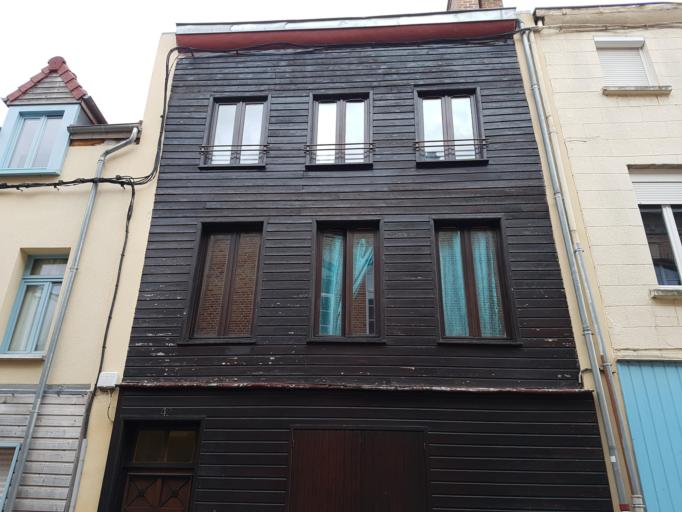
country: FR
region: Picardie
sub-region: Departement de la Somme
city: Amiens
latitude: 49.8997
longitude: 2.3019
